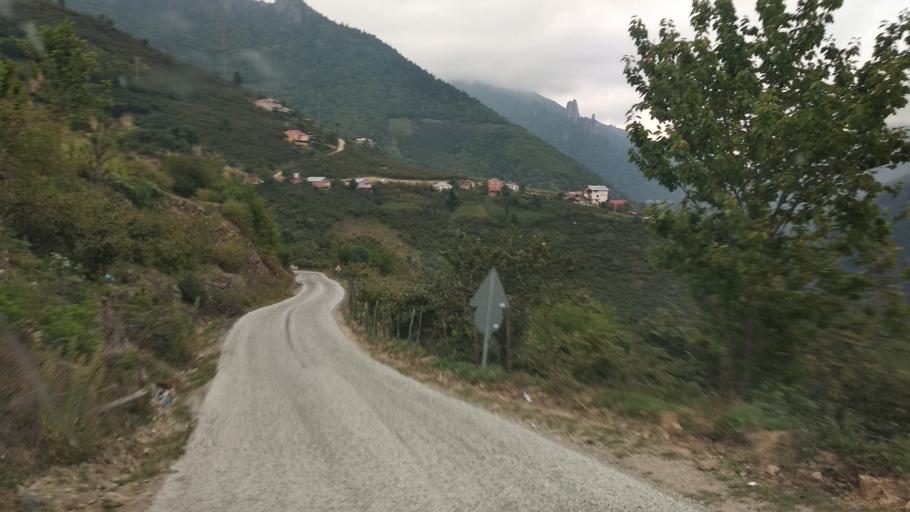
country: TR
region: Giresun
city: Dogankent
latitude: 40.7430
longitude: 38.9916
